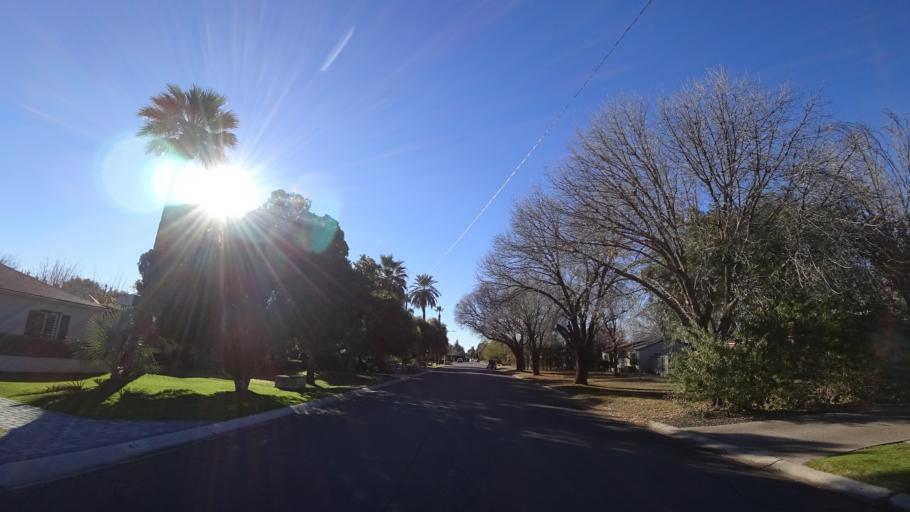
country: US
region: Arizona
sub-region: Maricopa County
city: Phoenix
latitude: 33.5129
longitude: -112.0710
